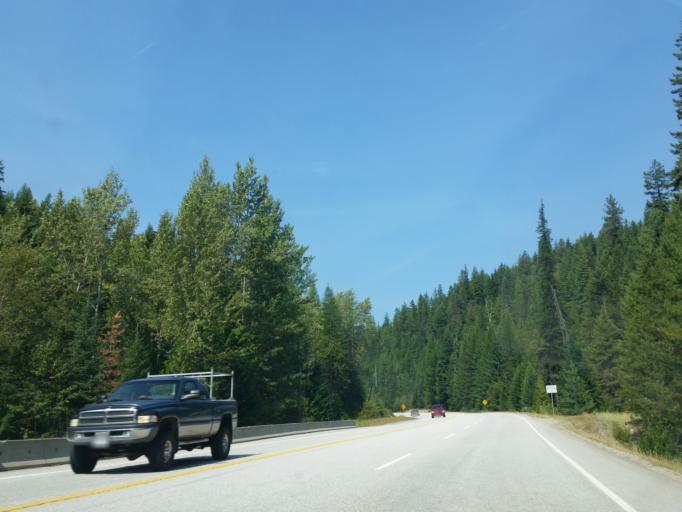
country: CA
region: British Columbia
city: Castlegar
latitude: 49.2771
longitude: -117.7207
